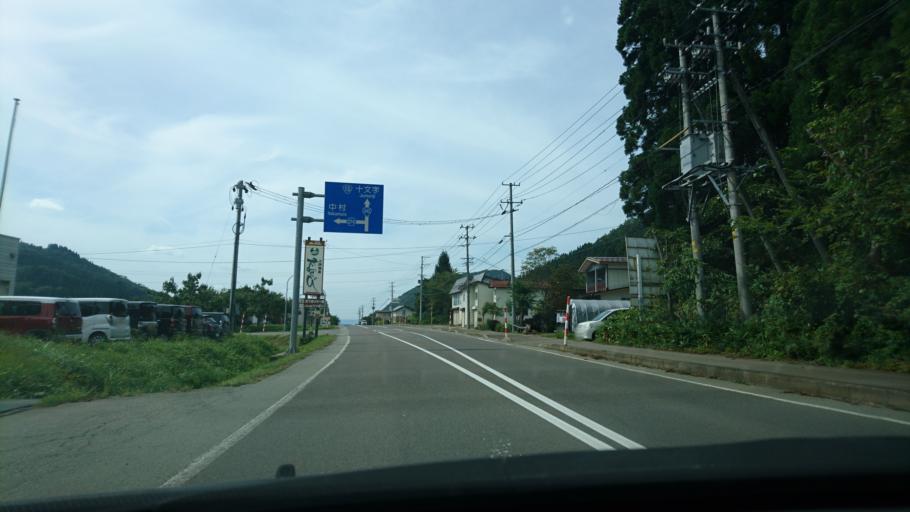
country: JP
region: Akita
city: Yuzawa
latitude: 39.1982
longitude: 140.6079
